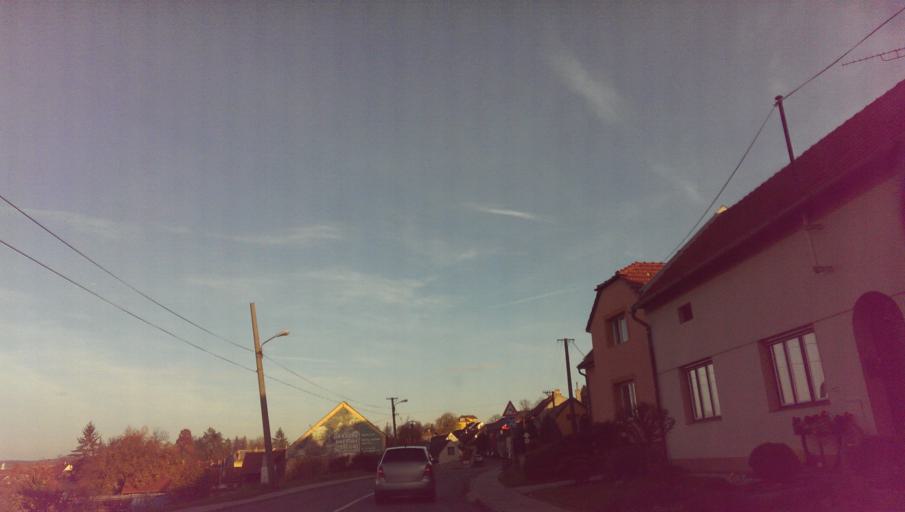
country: CZ
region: Zlin
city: Bilovice
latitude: 49.0980
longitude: 17.5435
